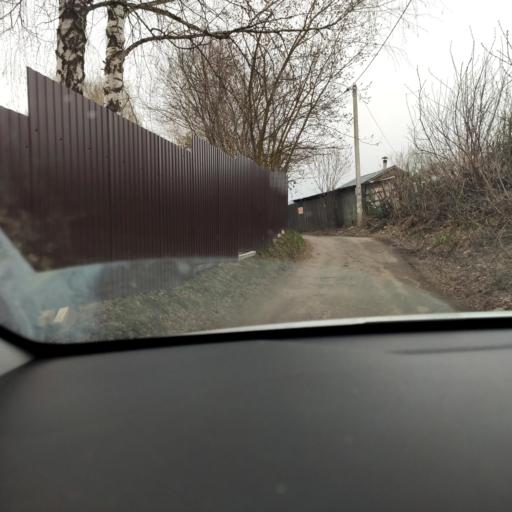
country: RU
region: Tatarstan
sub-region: Gorod Kazan'
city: Kazan
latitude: 55.8923
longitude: 49.0798
